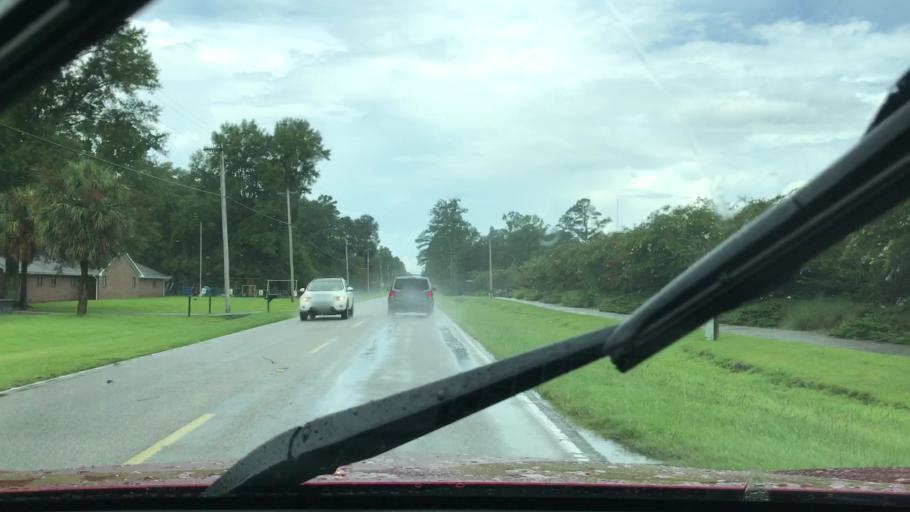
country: US
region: South Carolina
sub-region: Horry County
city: Red Hill
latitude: 33.8572
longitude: -79.0029
